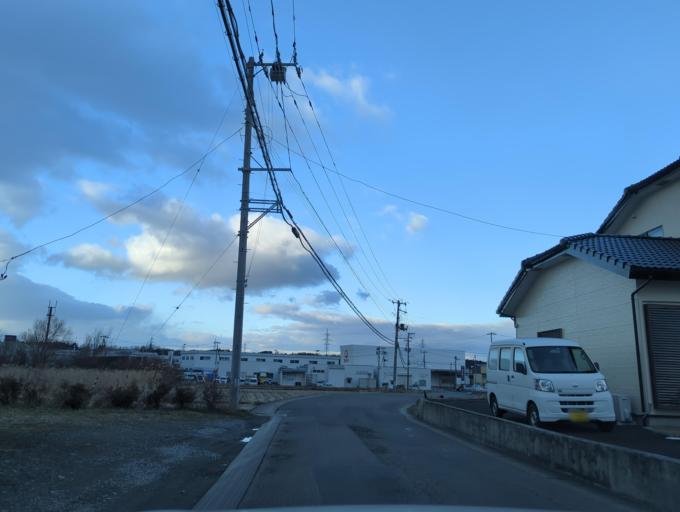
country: JP
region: Fukushima
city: Koriyama
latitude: 37.4231
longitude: 140.4034
